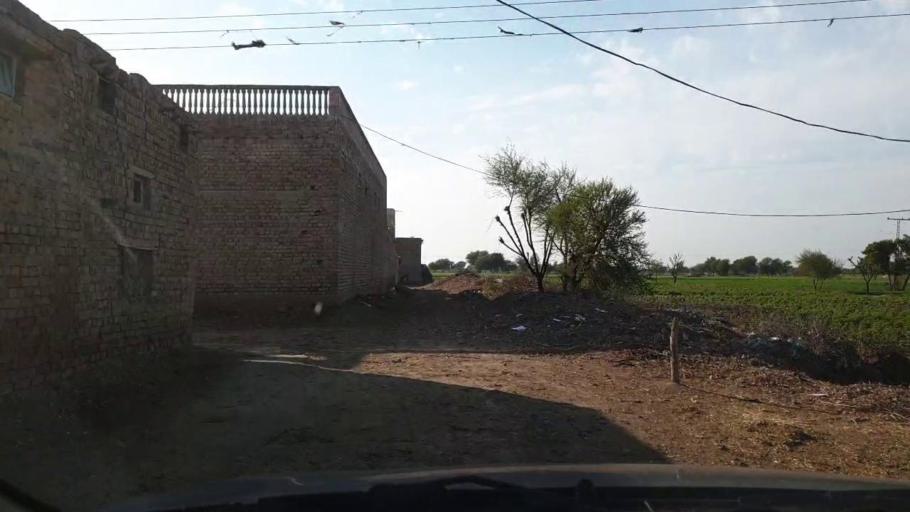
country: PK
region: Sindh
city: Jhol
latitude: 25.9782
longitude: 68.8381
